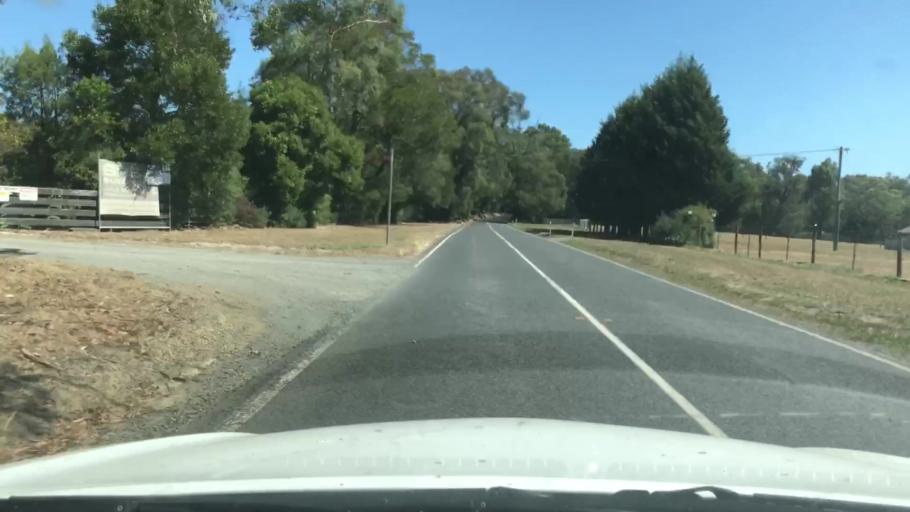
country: AU
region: Victoria
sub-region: Yarra Ranges
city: Woori Yallock
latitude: -37.8220
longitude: 145.4953
